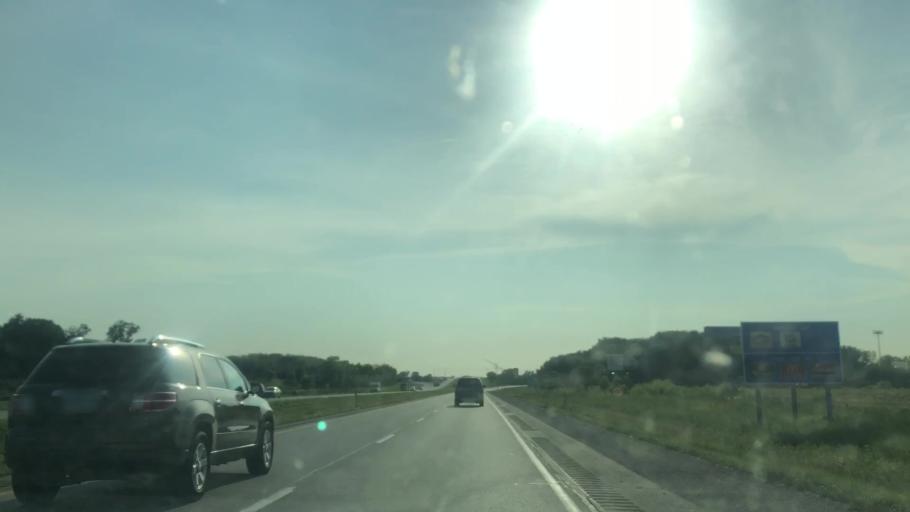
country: US
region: Iowa
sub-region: Story County
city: Ames
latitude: 42.0059
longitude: -93.5991
